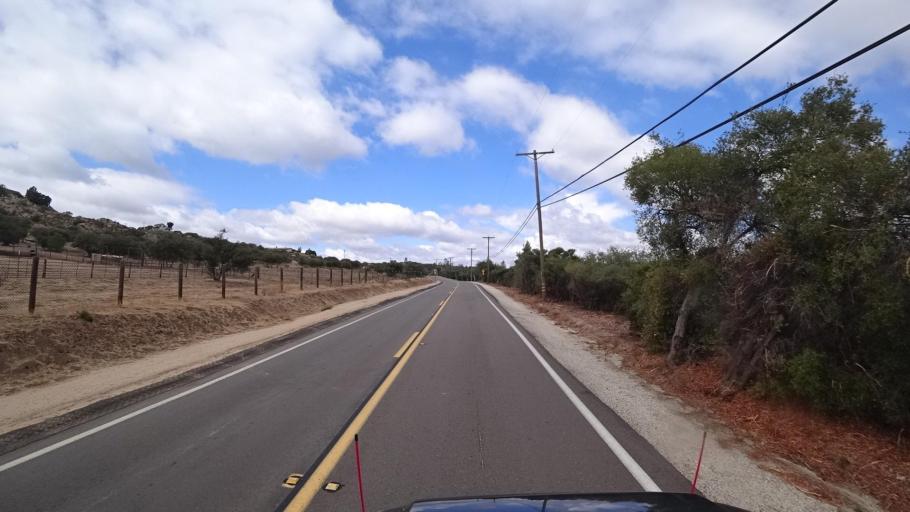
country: US
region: California
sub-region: San Diego County
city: Campo
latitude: 32.6678
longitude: -116.5019
